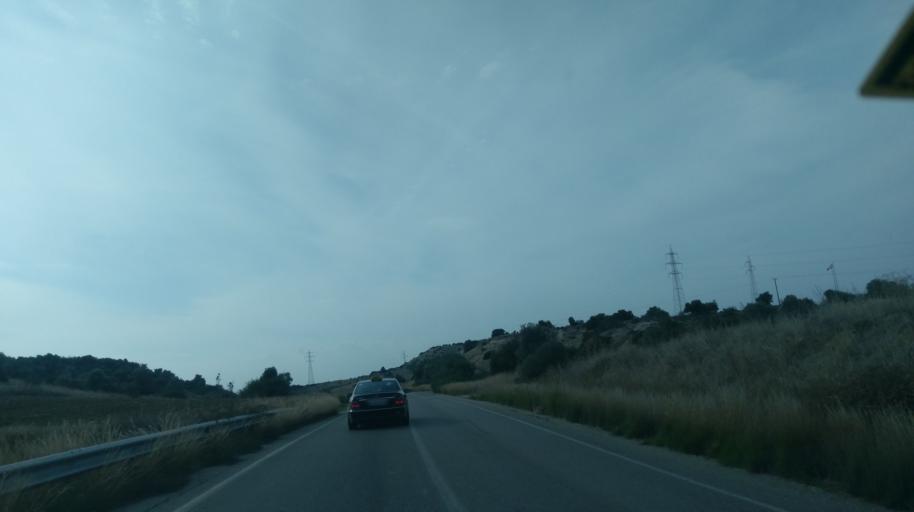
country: CY
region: Ammochostos
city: Leonarisso
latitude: 35.3906
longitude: 34.0583
